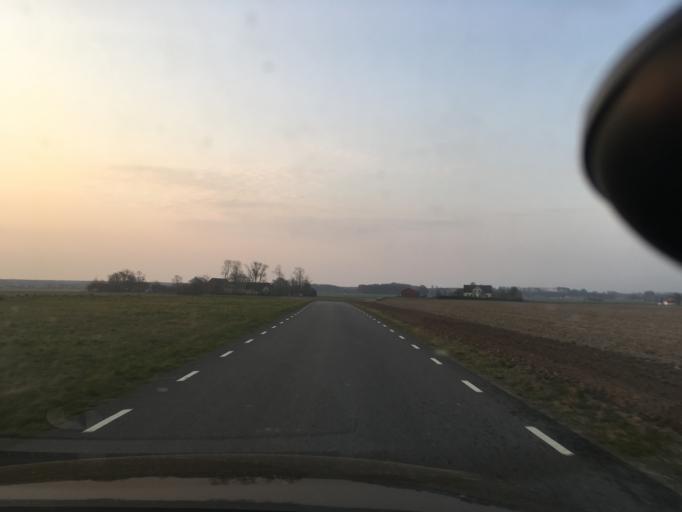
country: SE
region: Skane
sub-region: Ystads Kommun
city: Kopingebro
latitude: 55.4129
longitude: 14.1519
